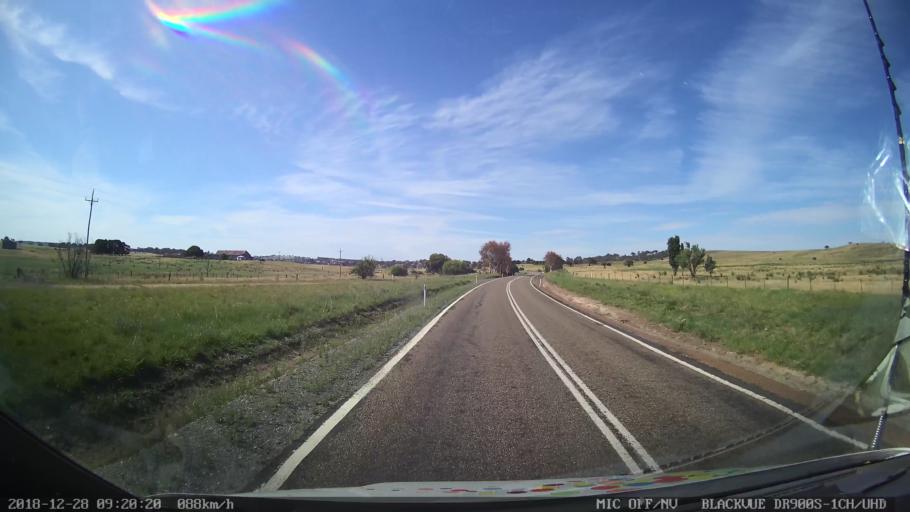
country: AU
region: New South Wales
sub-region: Upper Lachlan Shire
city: Crookwell
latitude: -34.3487
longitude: 149.3721
